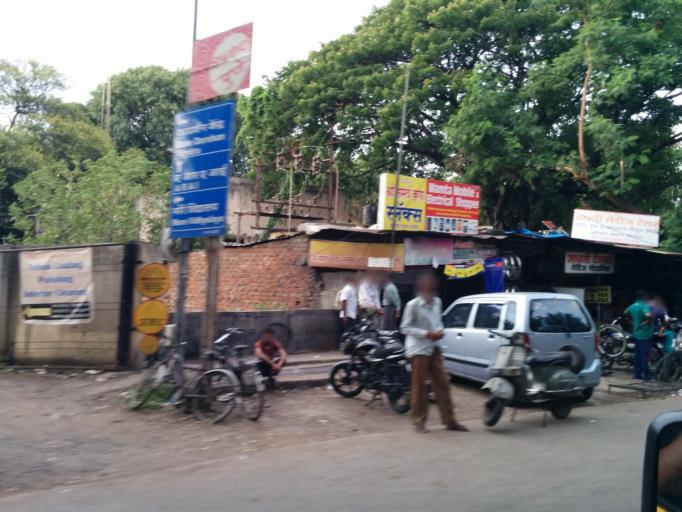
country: IN
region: Maharashtra
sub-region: Pune Division
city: Pune
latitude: 18.5110
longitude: 73.8194
